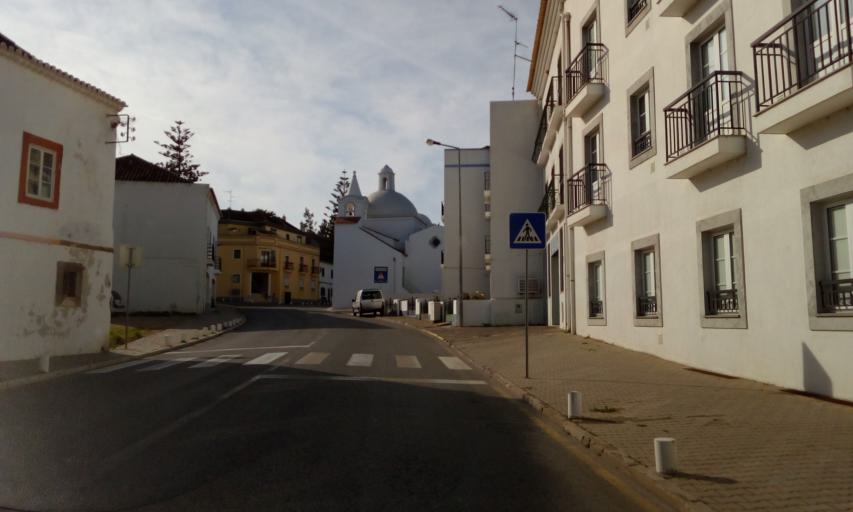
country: PT
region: Faro
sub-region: Tavira
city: Tavira
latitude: 37.1260
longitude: -7.6539
